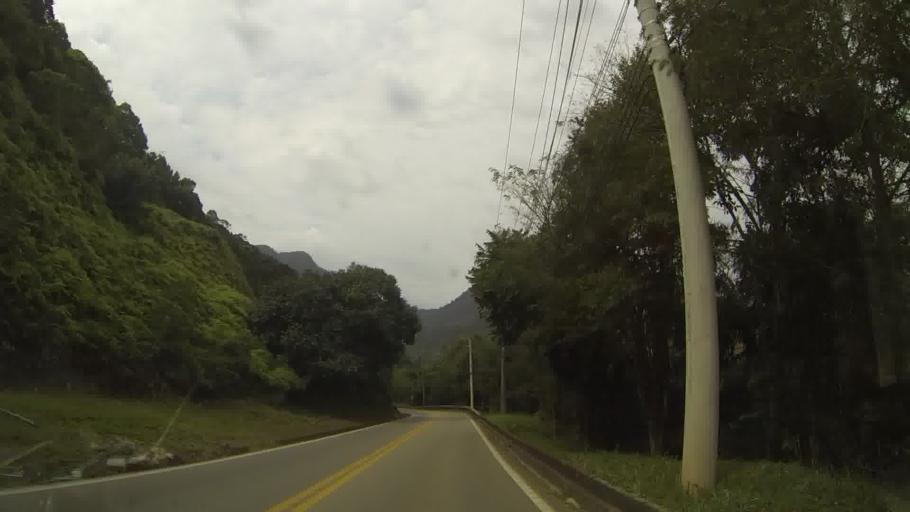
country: BR
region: Sao Paulo
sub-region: Sao Sebastiao
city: Sao Sebastiao
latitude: -23.7975
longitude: -45.5484
